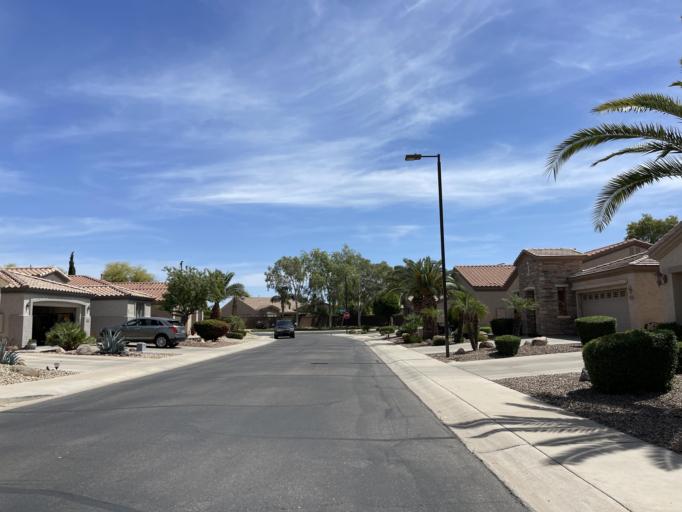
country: US
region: Arizona
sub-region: Maricopa County
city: Queen Creek
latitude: 33.2574
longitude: -111.7007
